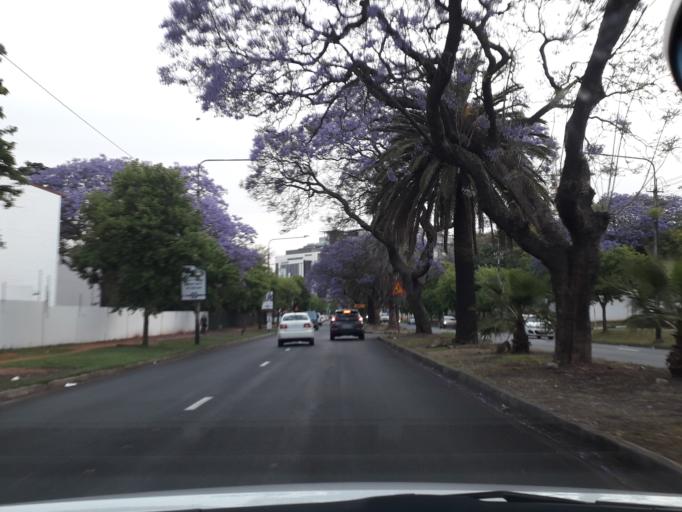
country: ZA
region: Gauteng
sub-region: City of Johannesburg Metropolitan Municipality
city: Johannesburg
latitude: -26.1393
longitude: 28.0453
